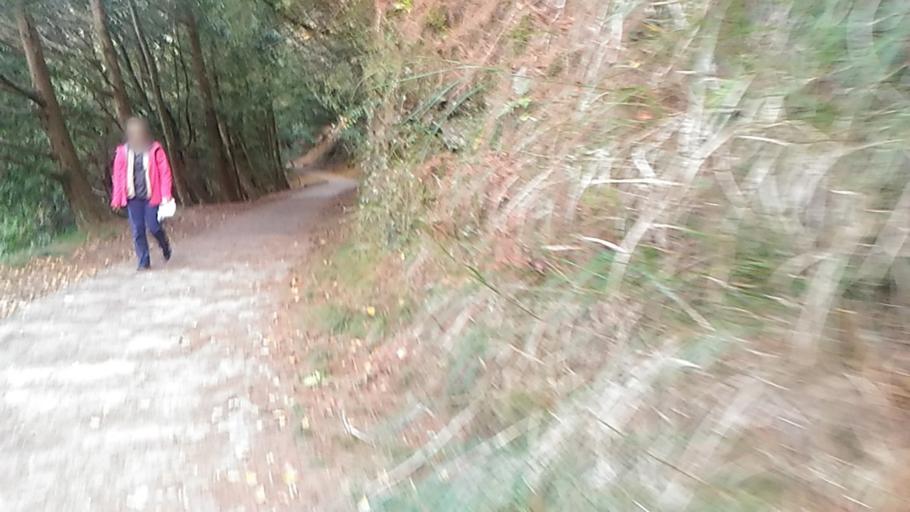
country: TW
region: Taiwan
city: Daxi
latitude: 24.4108
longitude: 121.3030
